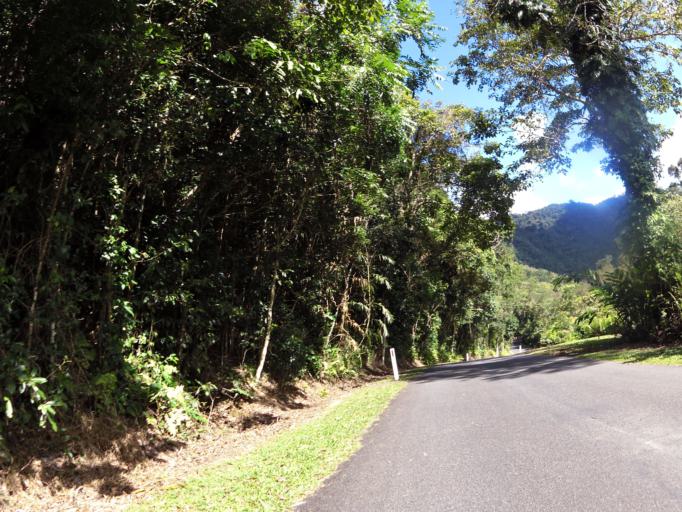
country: AU
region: Queensland
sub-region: Cairns
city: Woree
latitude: -16.9588
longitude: 145.6834
